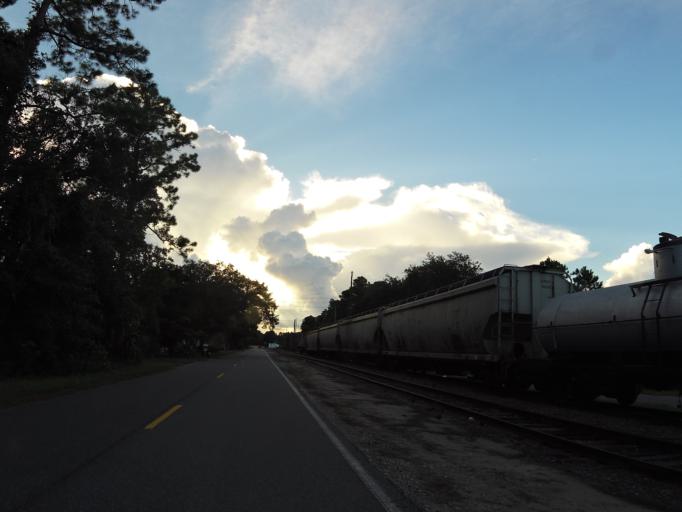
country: US
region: Georgia
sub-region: Camden County
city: St. Marys
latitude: 30.7351
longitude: -81.5474
